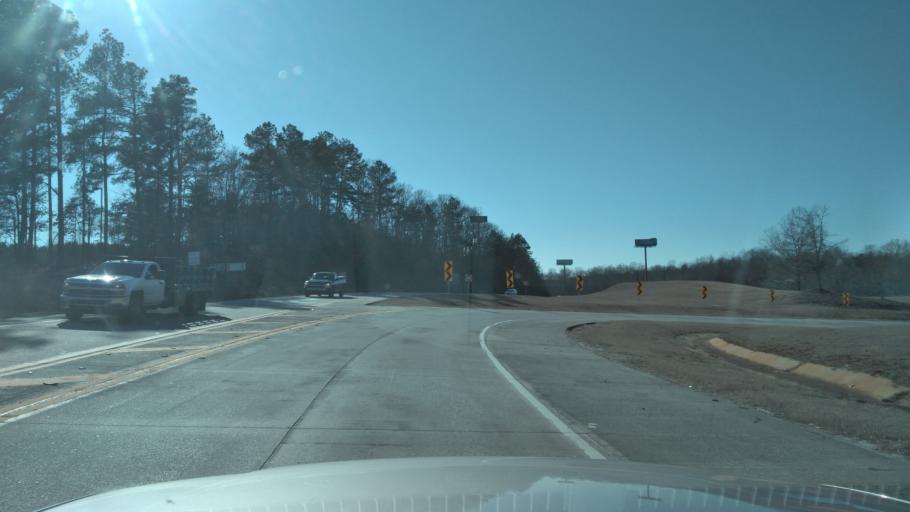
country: US
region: Georgia
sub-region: Jackson County
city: Commerce
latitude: 34.2282
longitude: -83.4996
